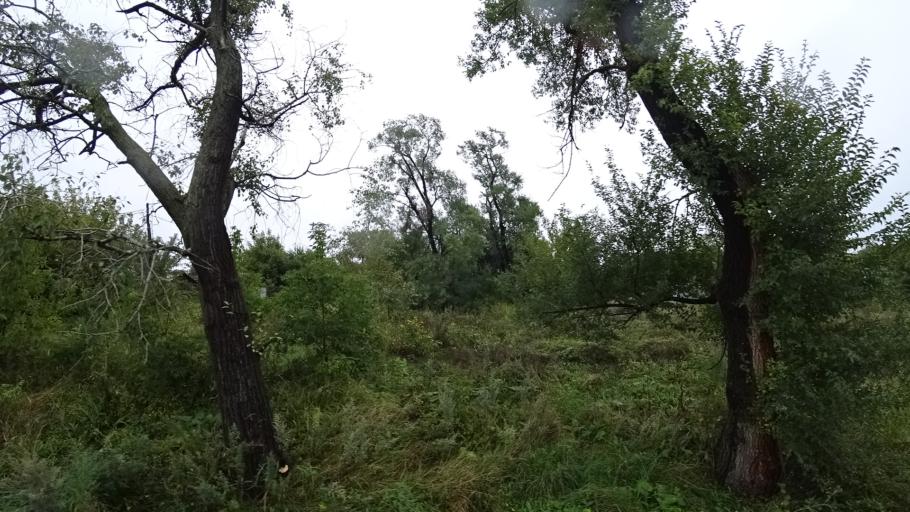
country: RU
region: Primorskiy
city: Monastyrishche
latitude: 44.1992
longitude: 132.4227
